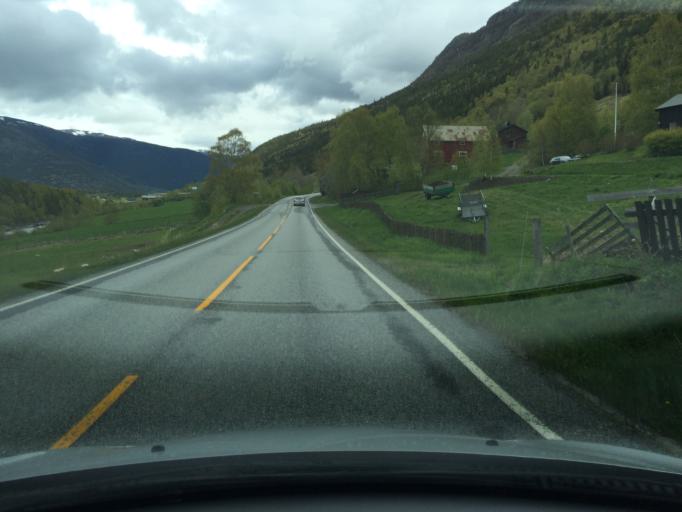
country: NO
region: Oppland
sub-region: Lom
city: Fossbergom
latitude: 61.8196
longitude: 8.5301
